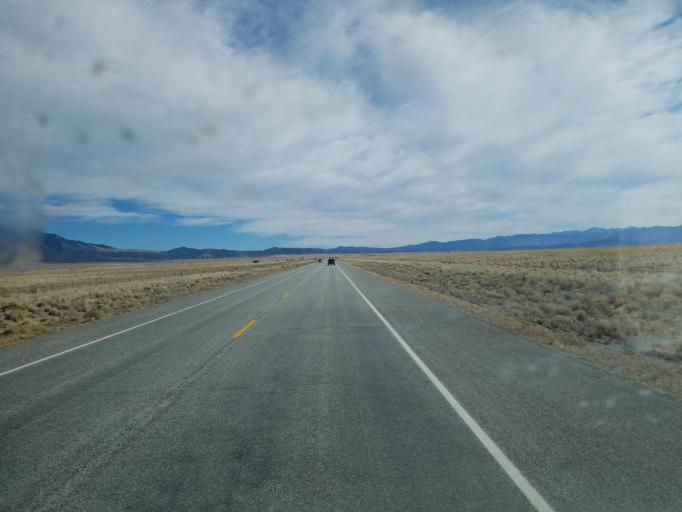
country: US
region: Colorado
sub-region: Alamosa County
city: Alamosa East
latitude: 37.4750
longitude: -105.6180
